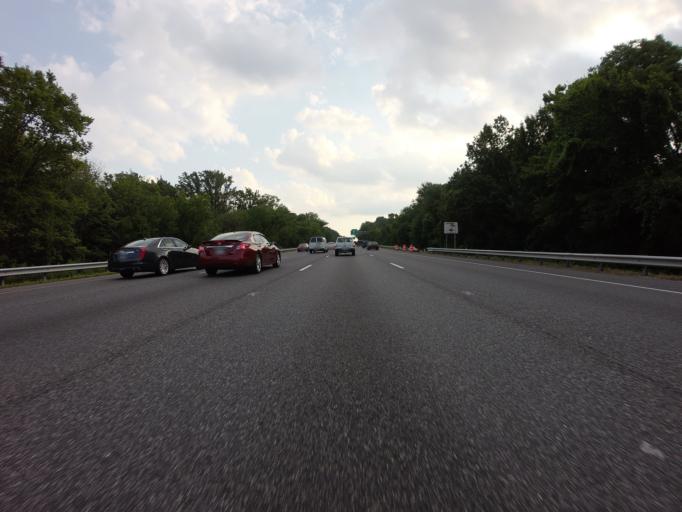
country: US
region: Maryland
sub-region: Anne Arundel County
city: Jessup
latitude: 39.1854
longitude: -76.7800
